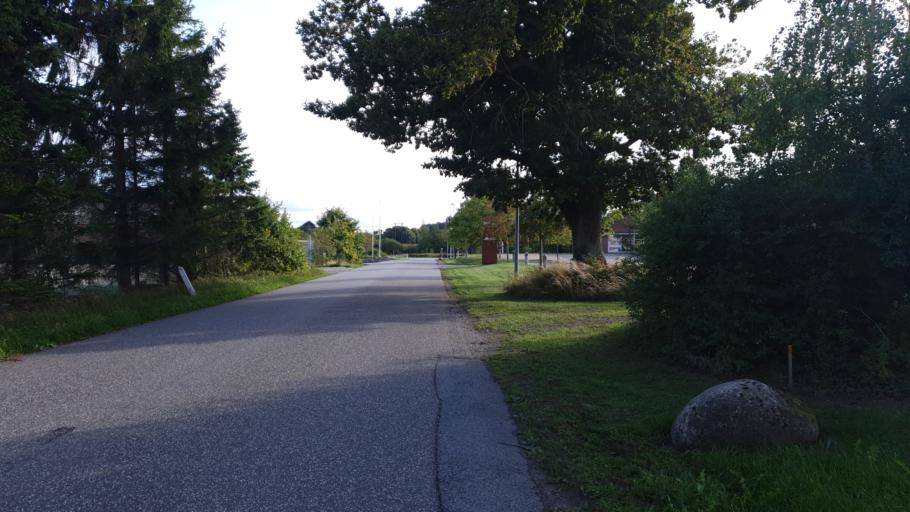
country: DK
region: South Denmark
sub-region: Fredericia Kommune
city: Snoghoj
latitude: 55.5446
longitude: 9.6895
